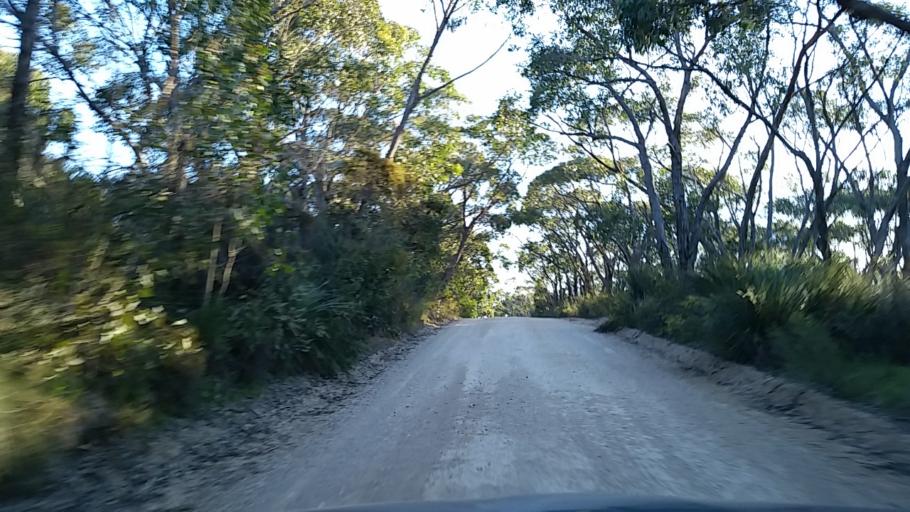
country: AU
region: South Australia
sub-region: Alexandrina
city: Mount Compass
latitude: -35.3022
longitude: 138.6790
